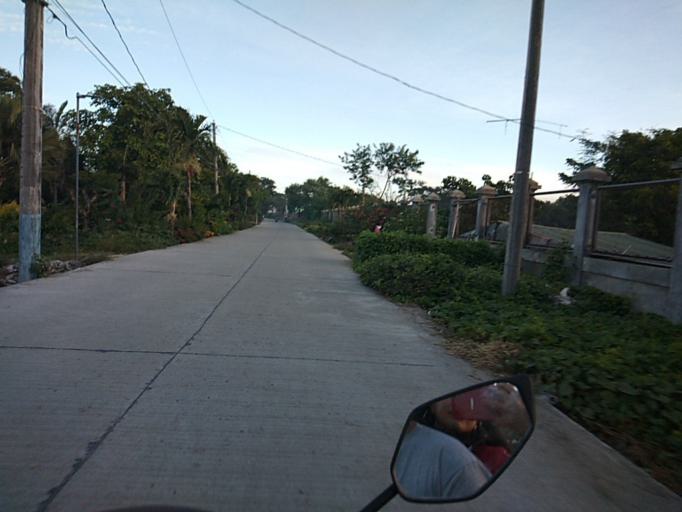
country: PH
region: Central Luzon
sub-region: Province of Bulacan
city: Balite
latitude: 14.8638
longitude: 120.7661
